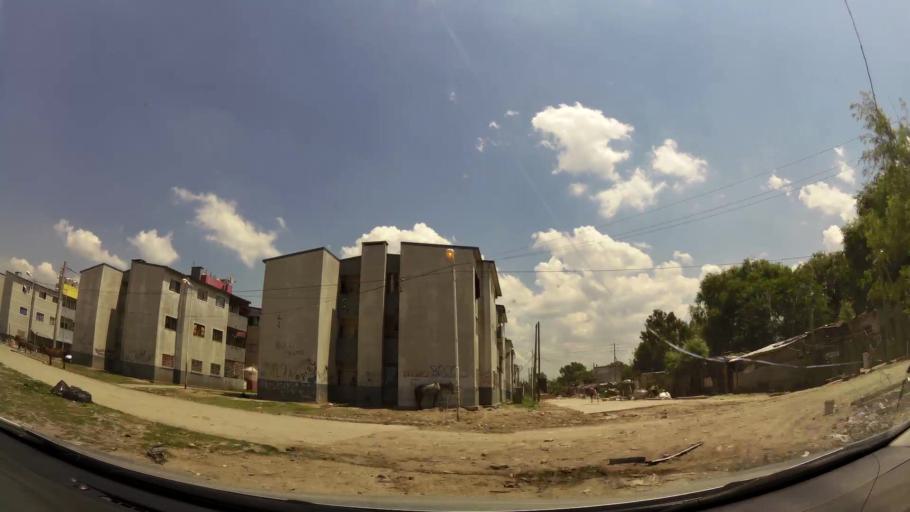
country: AR
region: Buenos Aires
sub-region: Partido de Tigre
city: Tigre
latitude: -34.4565
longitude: -58.6002
